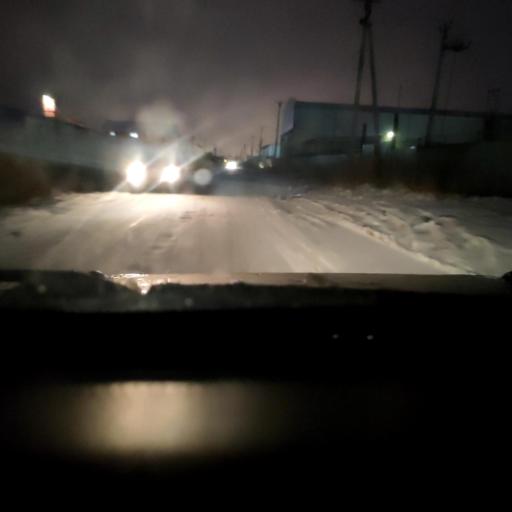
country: RU
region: Perm
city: Kondratovo
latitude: 57.9529
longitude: 56.0844
